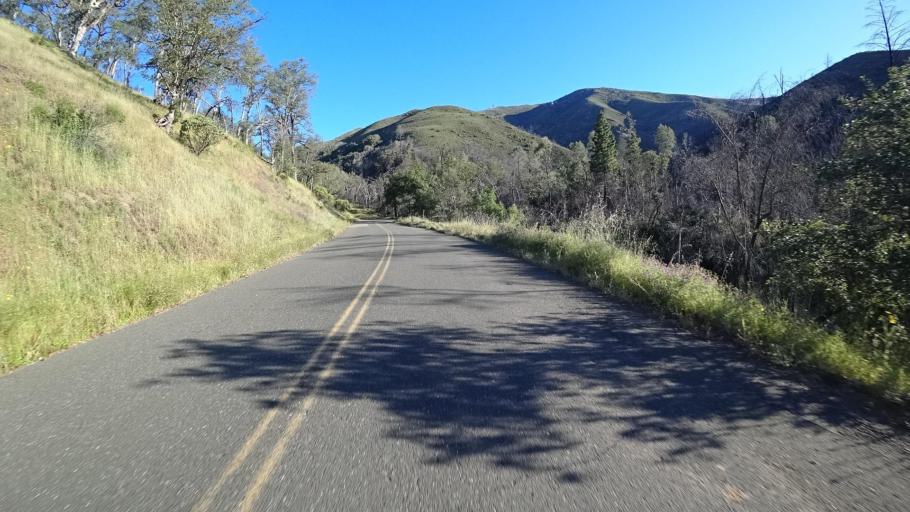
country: US
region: California
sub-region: Lake County
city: Upper Lake
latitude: 39.2572
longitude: -122.9475
